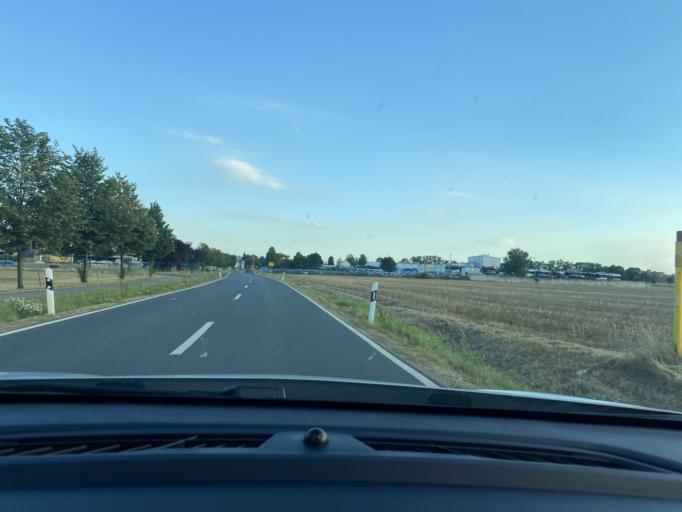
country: DE
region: Saxony
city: Kodersdorf
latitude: 51.2512
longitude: 14.8892
